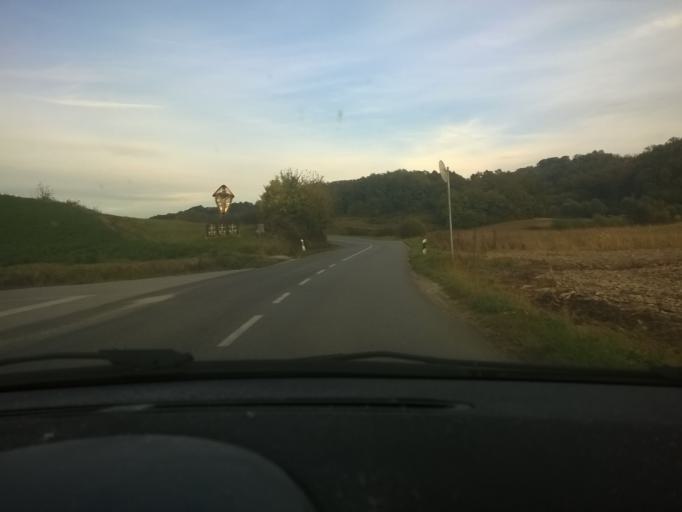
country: HR
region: Krapinsko-Zagorska
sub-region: Grad Krapina
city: Krapina
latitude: 46.1080
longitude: 15.8702
